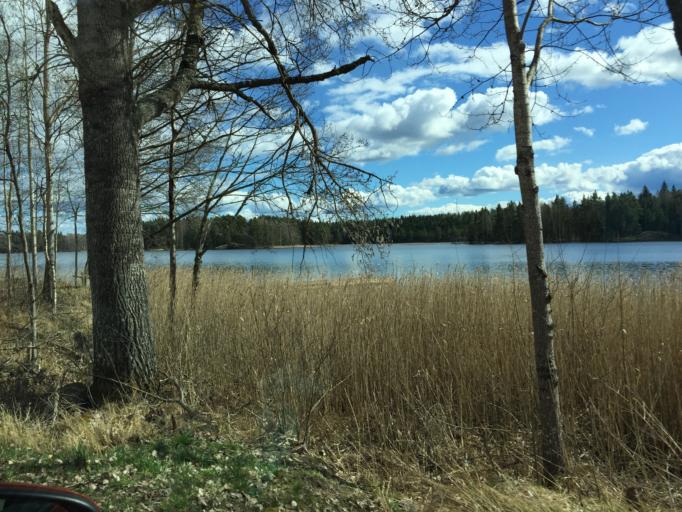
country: SE
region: Soedermanland
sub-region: Vingakers Kommun
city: Vingaker
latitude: 58.9325
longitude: 15.8328
